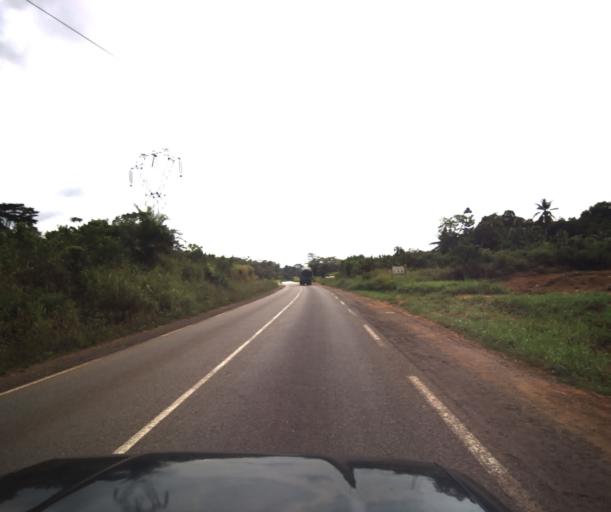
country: CM
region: Littoral
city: Edea
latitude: 3.8156
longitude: 10.3575
